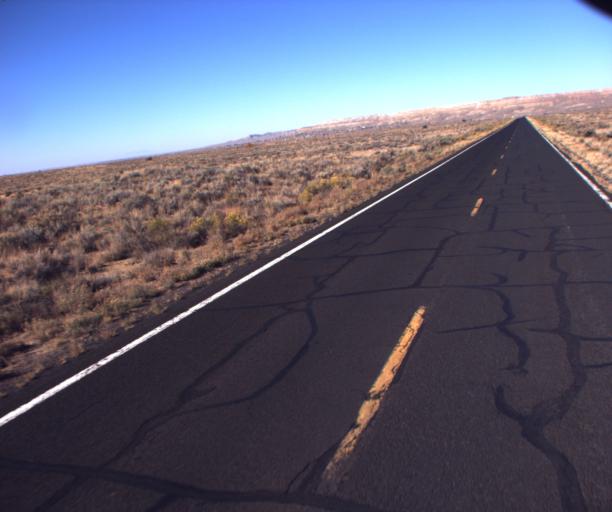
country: US
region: Arizona
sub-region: Navajo County
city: First Mesa
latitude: 35.8403
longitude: -110.3144
